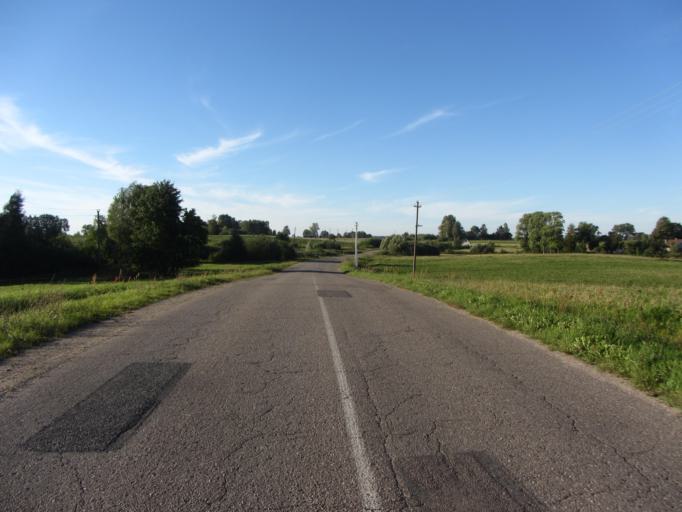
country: LT
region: Alytaus apskritis
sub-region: Alytus
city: Alytus
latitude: 54.4787
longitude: 24.0349
